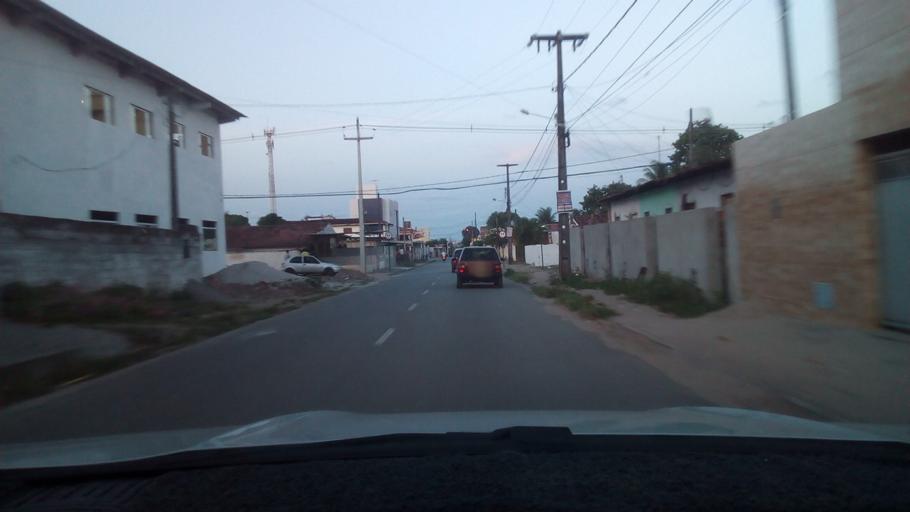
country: BR
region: Paraiba
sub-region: Bayeux
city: Bayeux
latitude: -7.1785
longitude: -34.9200
